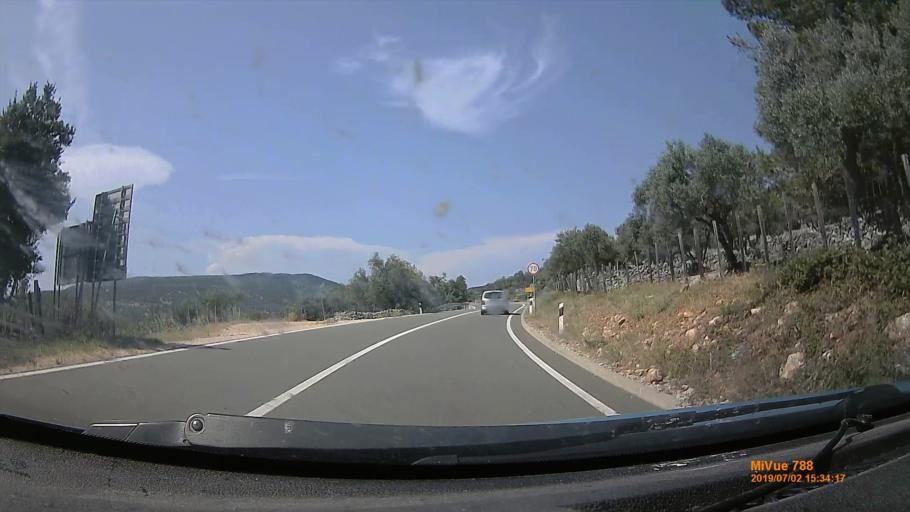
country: HR
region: Primorsko-Goranska
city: Cres
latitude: 44.9656
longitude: 14.4127
